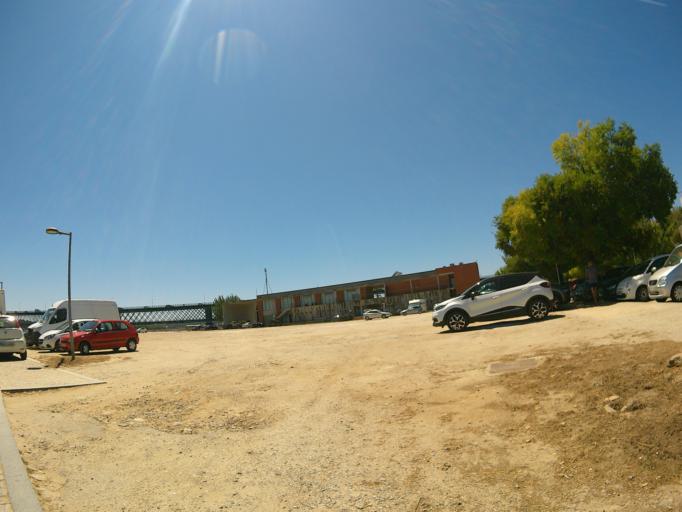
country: PT
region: Viana do Castelo
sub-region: Viana do Castelo
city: Viana do Castelo
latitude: 41.6953
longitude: -8.8185
